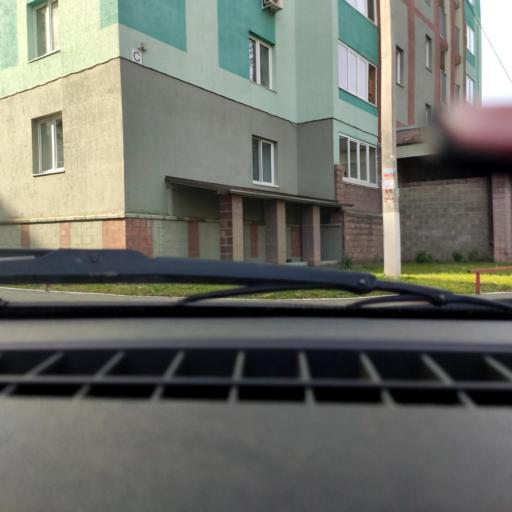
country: RU
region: Bashkortostan
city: Ufa
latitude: 54.7617
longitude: 56.0627
